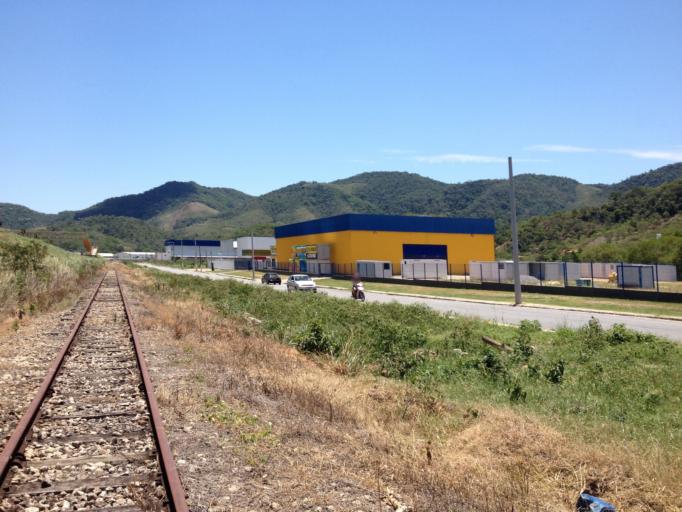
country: BR
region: Rio de Janeiro
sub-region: Rio Bonito
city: Rio Bonito
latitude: -22.7069
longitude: -42.6532
